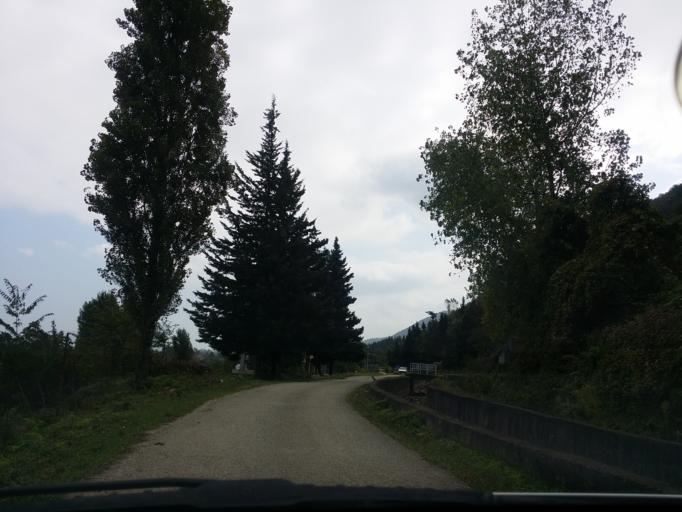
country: IR
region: Mazandaran
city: Chalus
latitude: 36.6528
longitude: 51.3490
